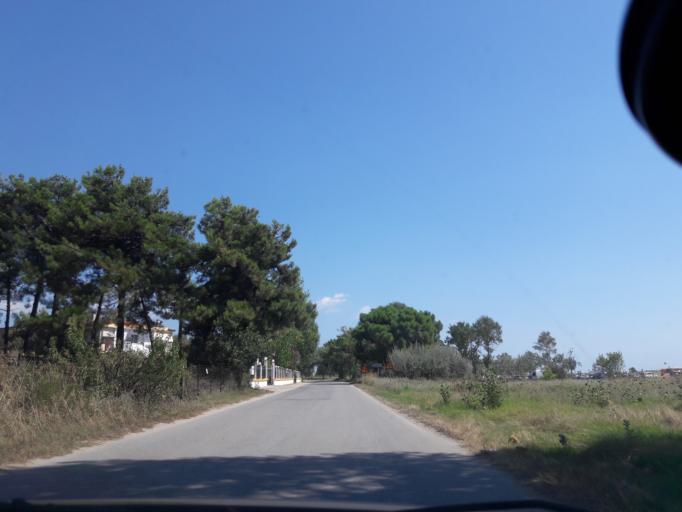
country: GR
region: Central Macedonia
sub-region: Nomos Chalkidikis
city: Nea Kallikrateia
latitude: 40.3371
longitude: 23.0201
